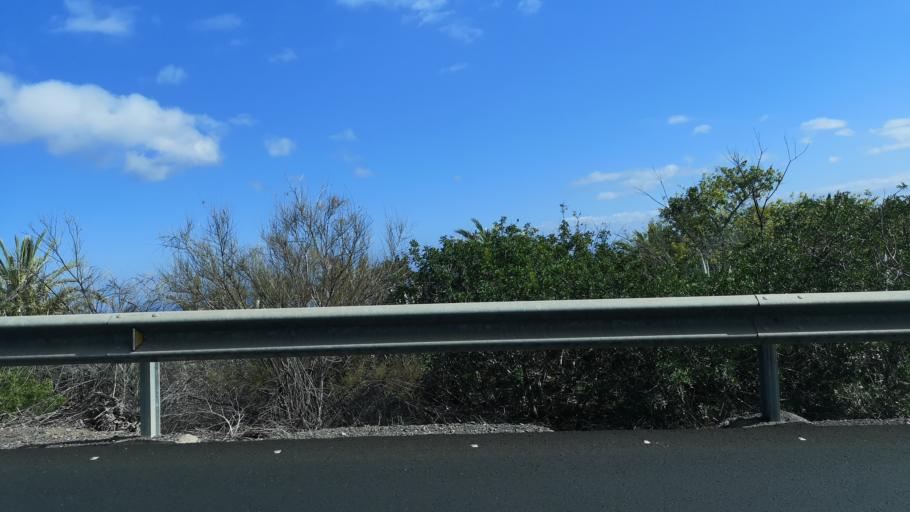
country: ES
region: Canary Islands
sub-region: Provincia de Santa Cruz de Tenerife
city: Alajero
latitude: 28.0423
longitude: -17.1943
